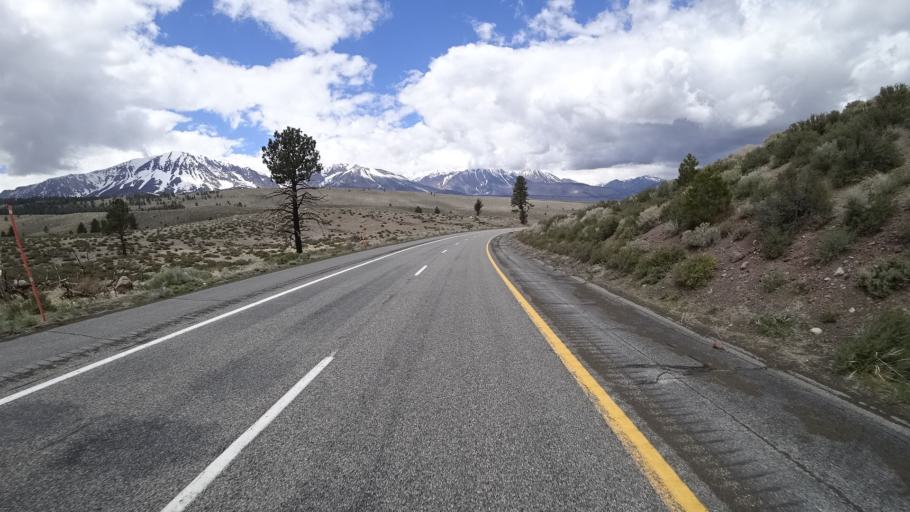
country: US
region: California
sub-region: Mono County
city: Mammoth Lakes
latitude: 37.8296
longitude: -119.0701
